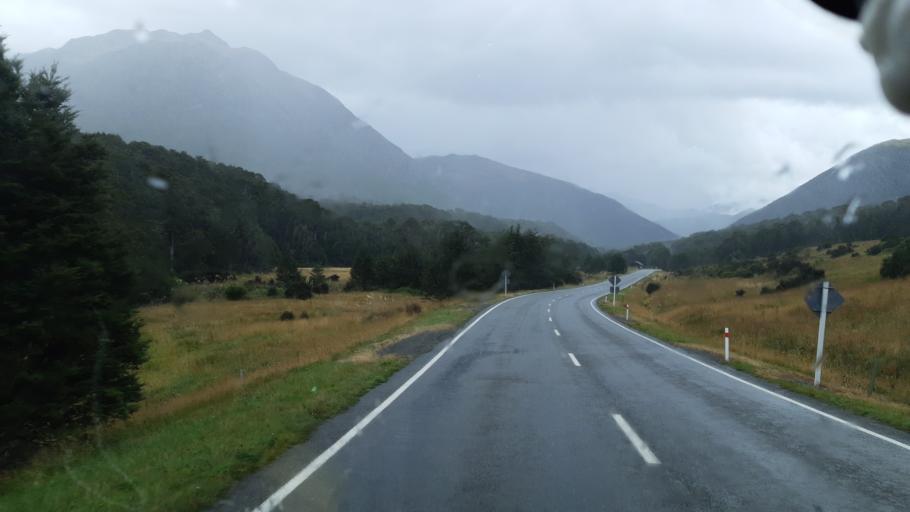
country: NZ
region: Canterbury
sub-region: Hurunui District
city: Amberley
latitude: -42.4257
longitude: 172.4019
